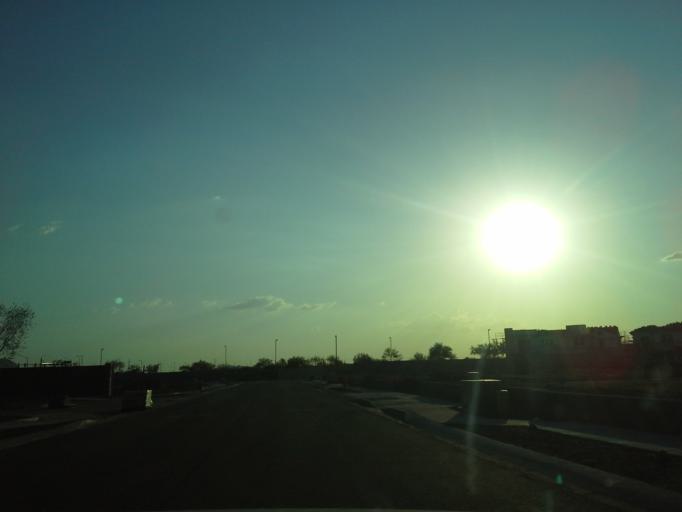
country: US
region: Arizona
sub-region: Maricopa County
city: Anthem
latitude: 33.7701
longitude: -112.1103
